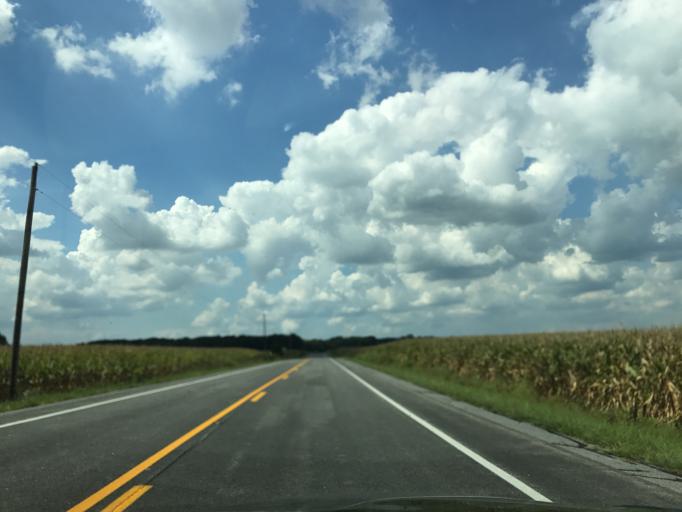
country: US
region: Maryland
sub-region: Queen Anne's County
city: Kingstown
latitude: 39.1407
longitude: -75.9069
